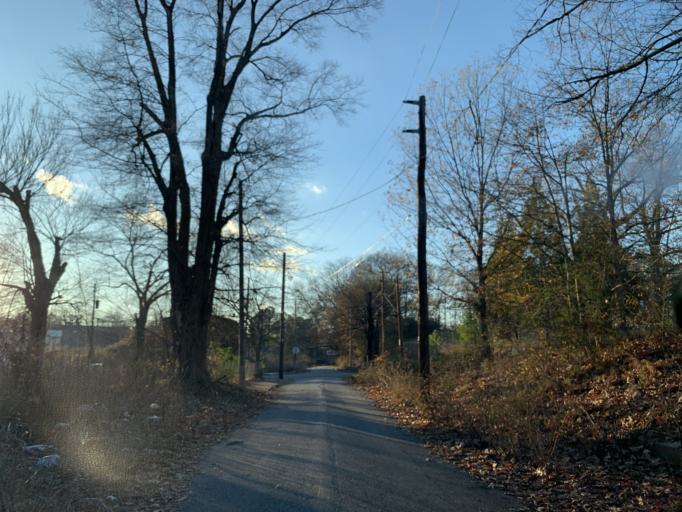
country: US
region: Georgia
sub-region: Fulton County
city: Atlanta
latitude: 33.7433
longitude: -84.3964
